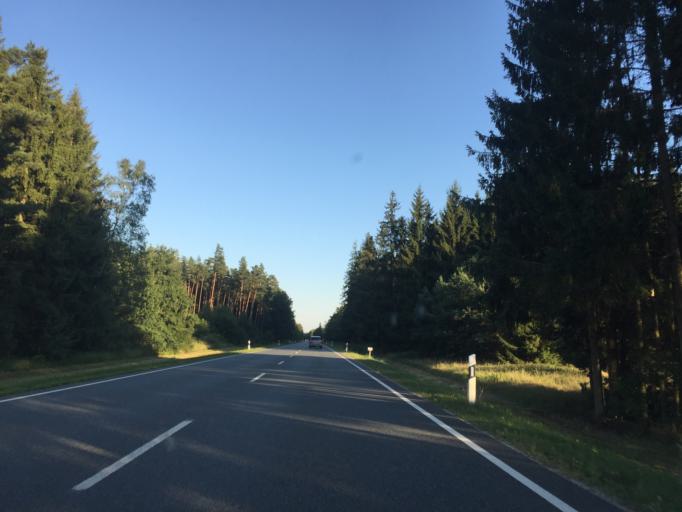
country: DE
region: Bavaria
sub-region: Upper Palatinate
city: Pressath
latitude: 49.7512
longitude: 11.9348
